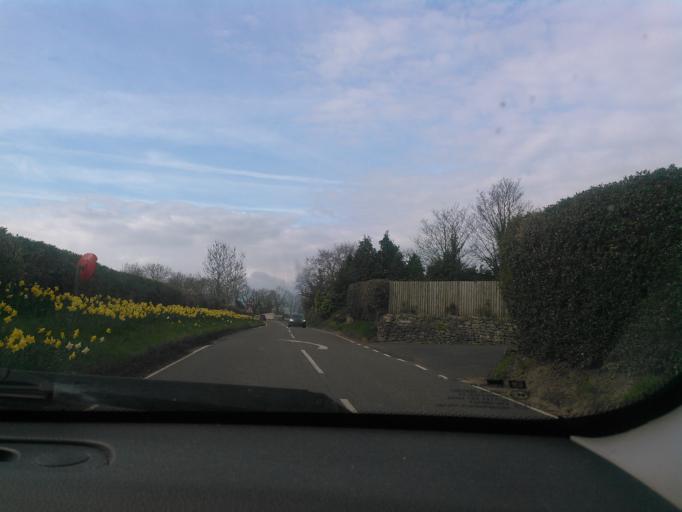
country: GB
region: England
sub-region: Shropshire
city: Bayston Hill
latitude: 52.6855
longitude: -2.7802
